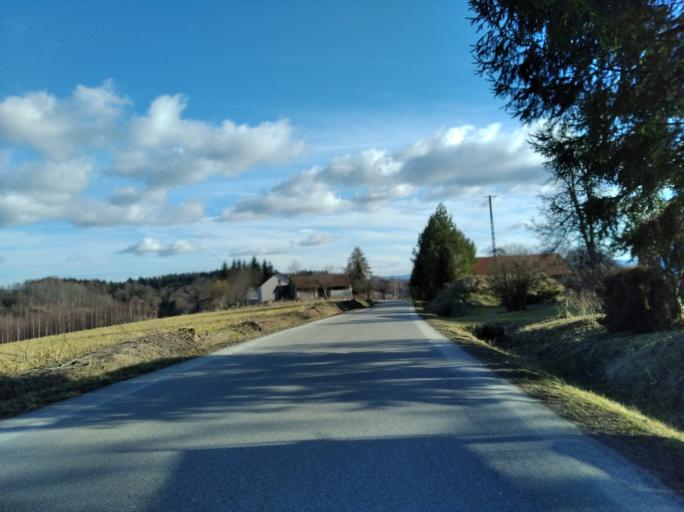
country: PL
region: Subcarpathian Voivodeship
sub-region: Powiat strzyzowski
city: Wisniowa
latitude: 49.8972
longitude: 21.7051
